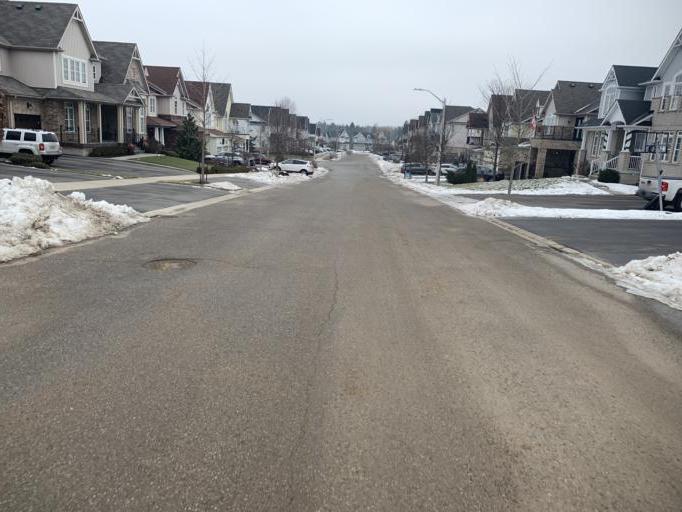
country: CA
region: Ontario
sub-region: Halton
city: Milton
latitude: 43.6605
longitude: -79.9247
